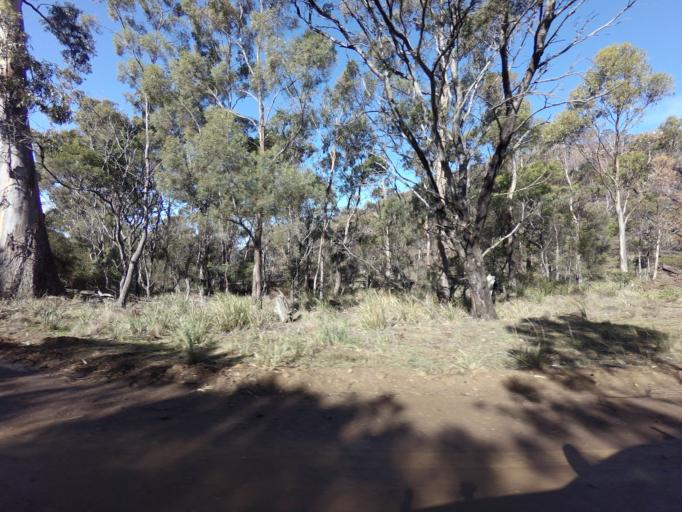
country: AU
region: Tasmania
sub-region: Sorell
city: Sorell
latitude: -42.4134
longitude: 147.9503
